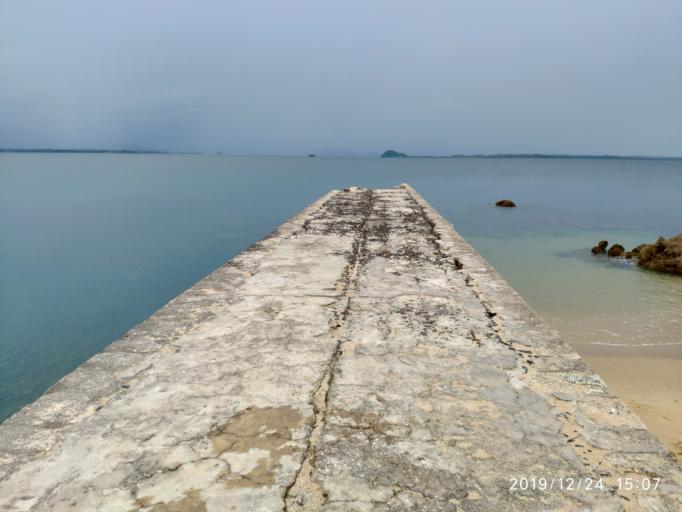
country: MG
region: Diana
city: Antsiranana
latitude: -12.2665
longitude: 49.3116
